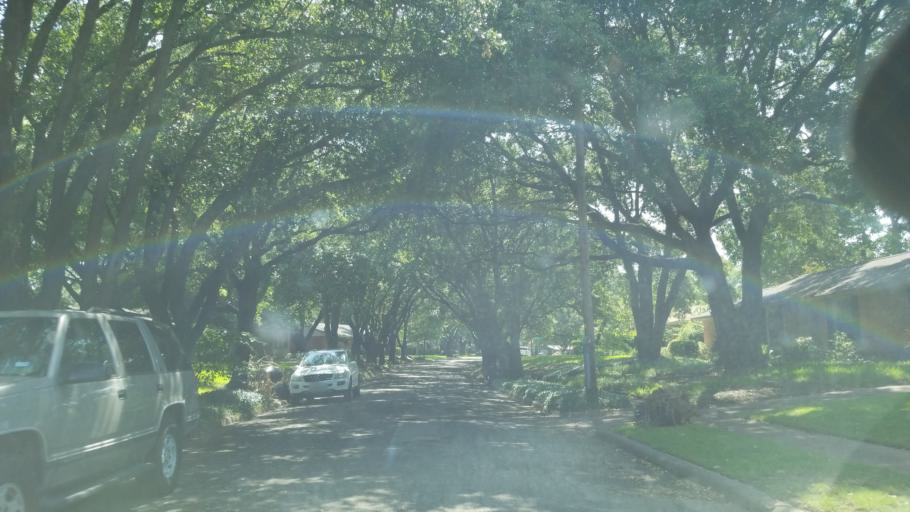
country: US
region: Texas
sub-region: Dallas County
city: Farmers Branch
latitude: 32.8885
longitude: -96.8603
